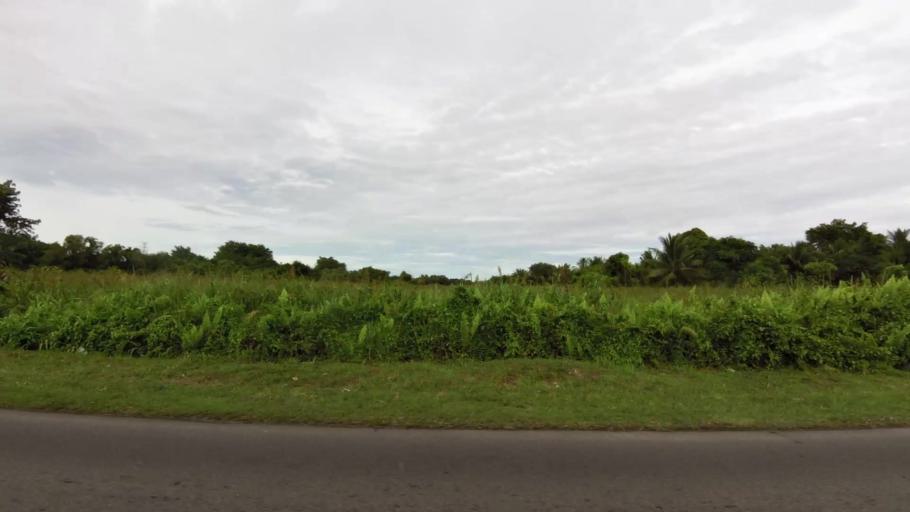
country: BN
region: Belait
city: Seria
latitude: 4.6038
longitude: 114.3256
